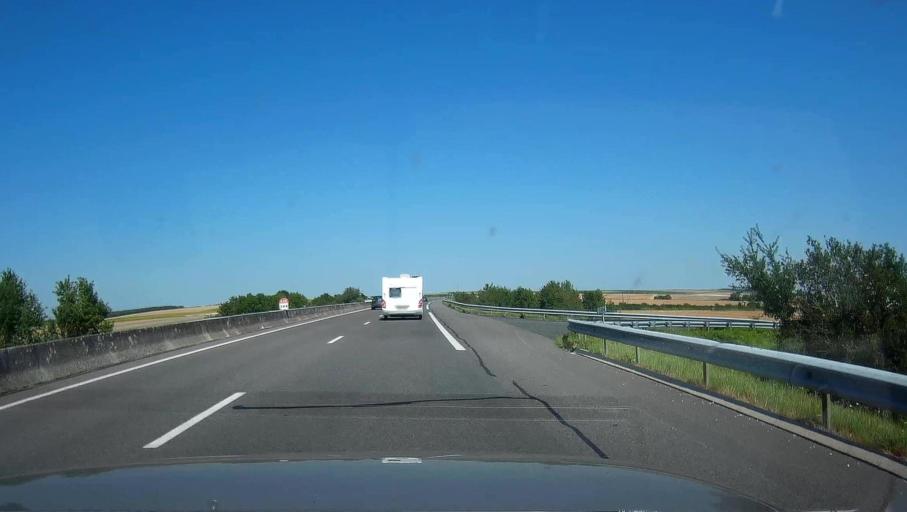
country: FR
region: Champagne-Ardenne
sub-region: Departement de l'Aube
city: Mailly-le-Camp
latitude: 48.6697
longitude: 4.1701
